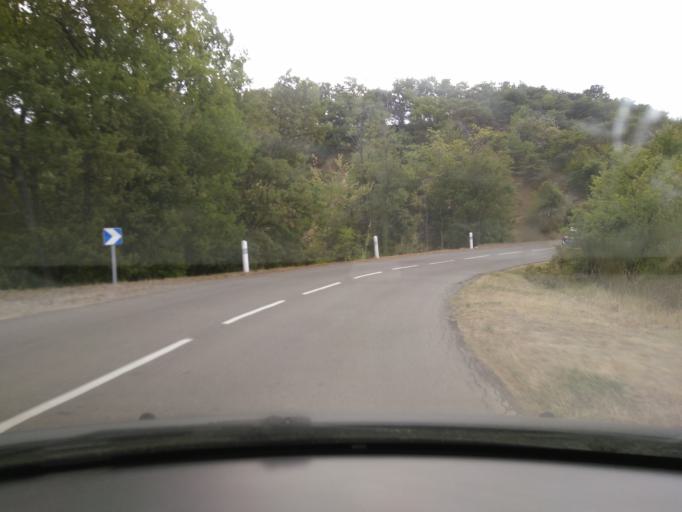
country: FR
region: Rhone-Alpes
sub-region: Departement de la Drome
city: Nyons
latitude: 44.4090
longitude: 5.0743
